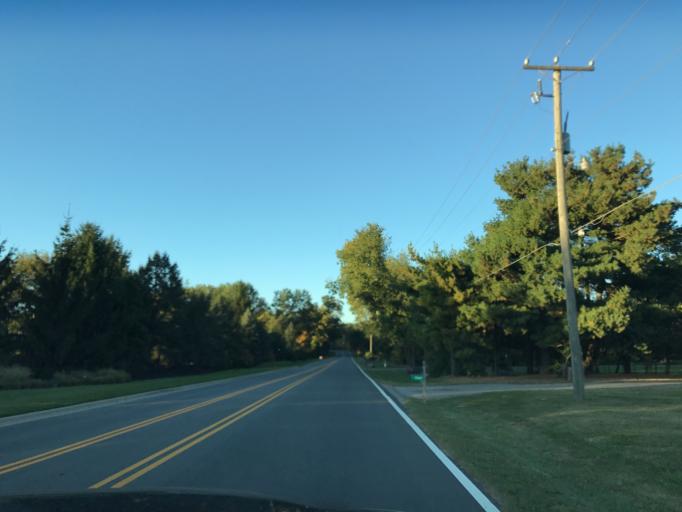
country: US
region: Ohio
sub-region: Franklin County
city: Westerville
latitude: 40.1602
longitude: -82.8788
